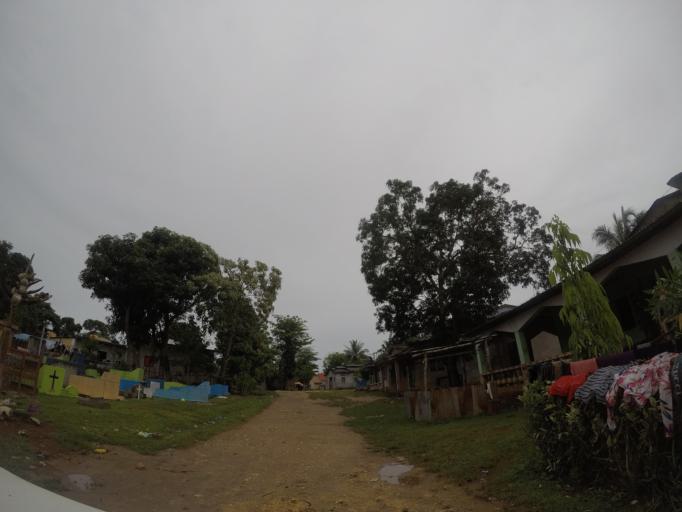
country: TL
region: Lautem
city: Lospalos
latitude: -8.5215
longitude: 127.0051
